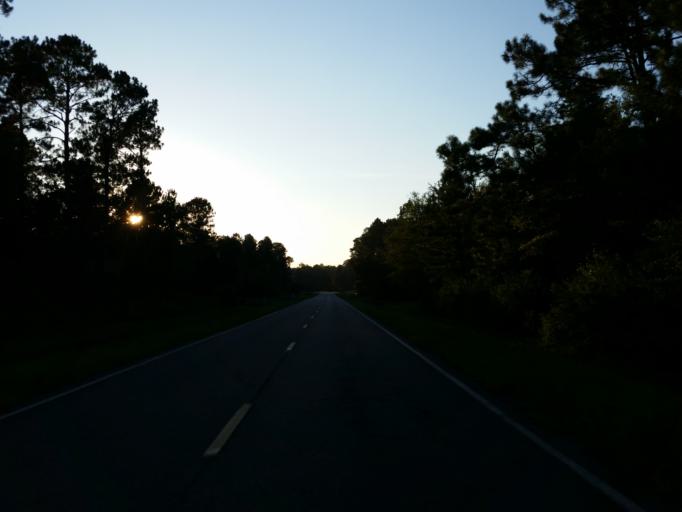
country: US
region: Georgia
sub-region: Berrien County
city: Nashville
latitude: 31.1834
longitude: -83.1440
